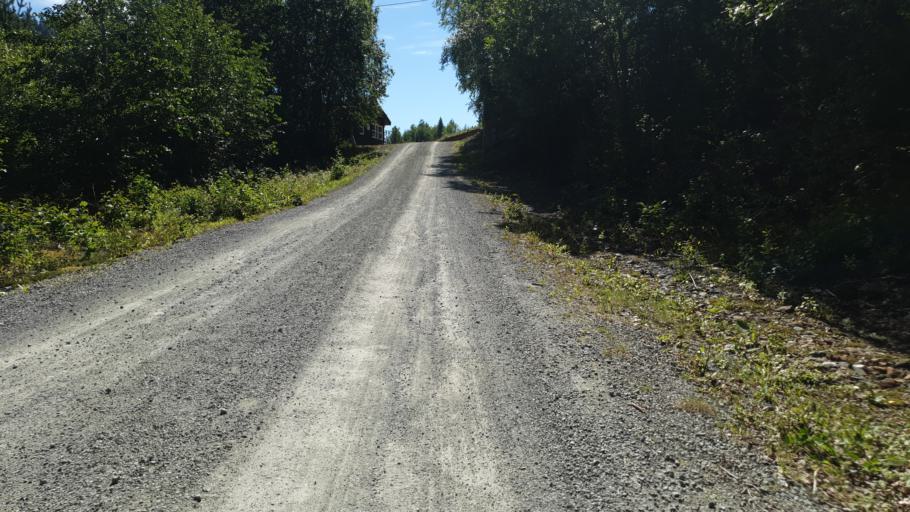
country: NO
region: Sor-Trondelag
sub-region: Meldal
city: Meldal
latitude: 63.1227
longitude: 9.7017
